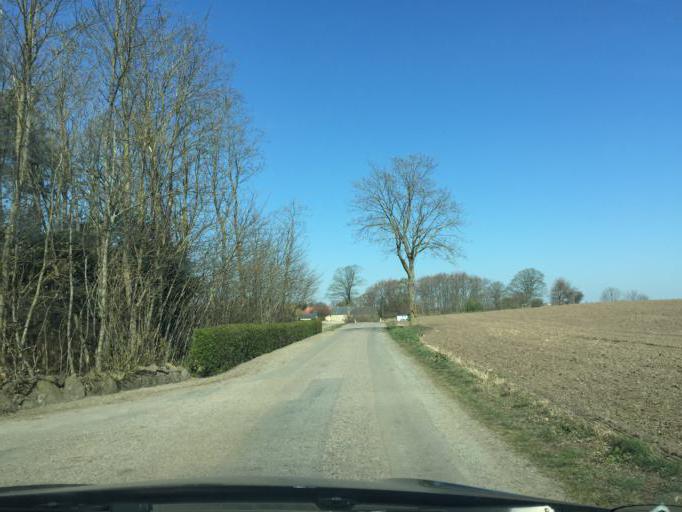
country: DK
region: South Denmark
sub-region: Faaborg-Midtfyn Kommune
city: Arslev
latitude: 55.2936
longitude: 10.5205
